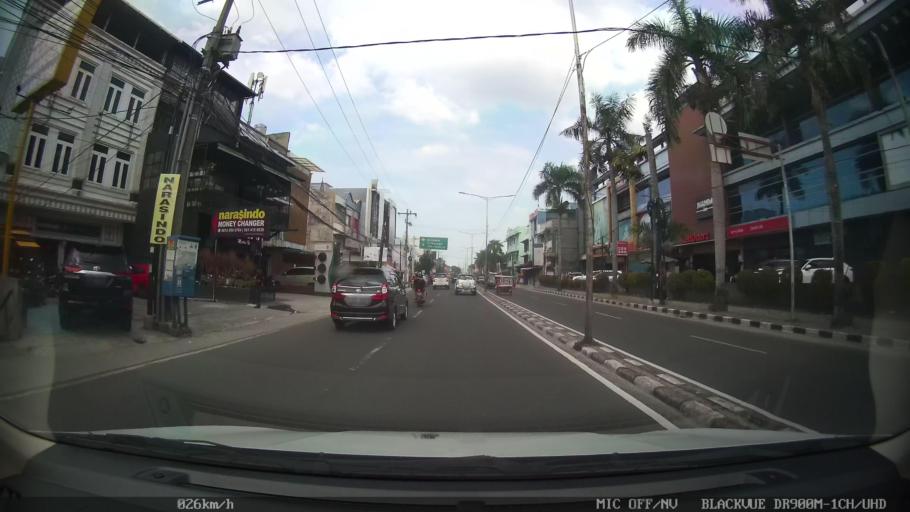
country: ID
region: North Sumatra
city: Medan
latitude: 3.5723
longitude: 98.6828
